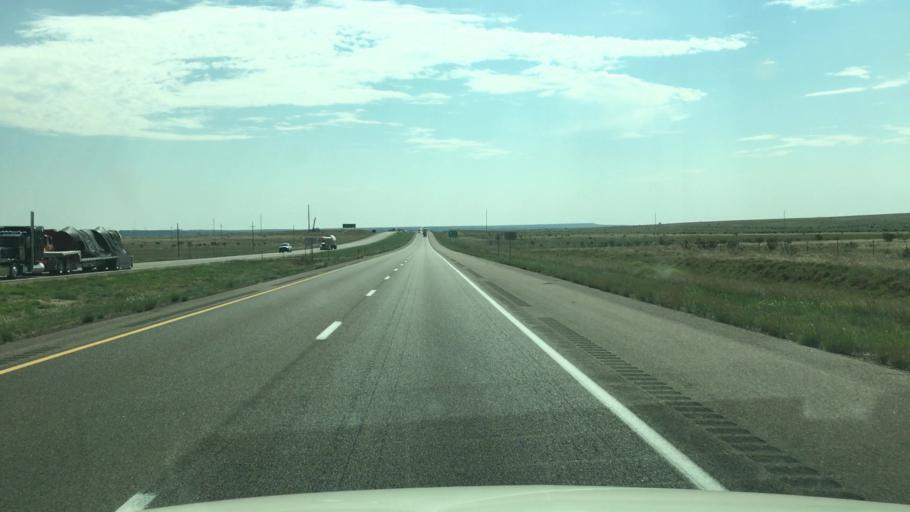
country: US
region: New Mexico
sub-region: Guadalupe County
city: Santa Rosa
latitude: 34.9785
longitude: -105.0337
